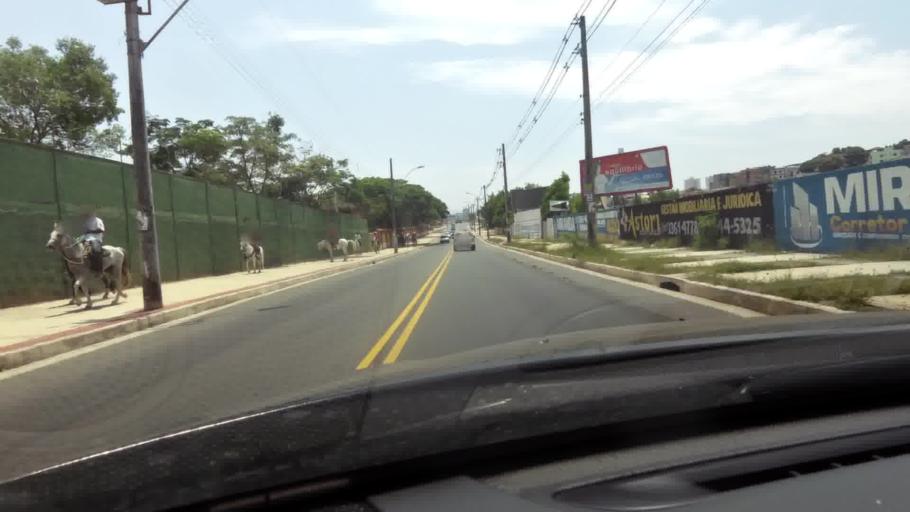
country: BR
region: Espirito Santo
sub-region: Guarapari
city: Guarapari
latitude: -20.6542
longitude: -40.5005
